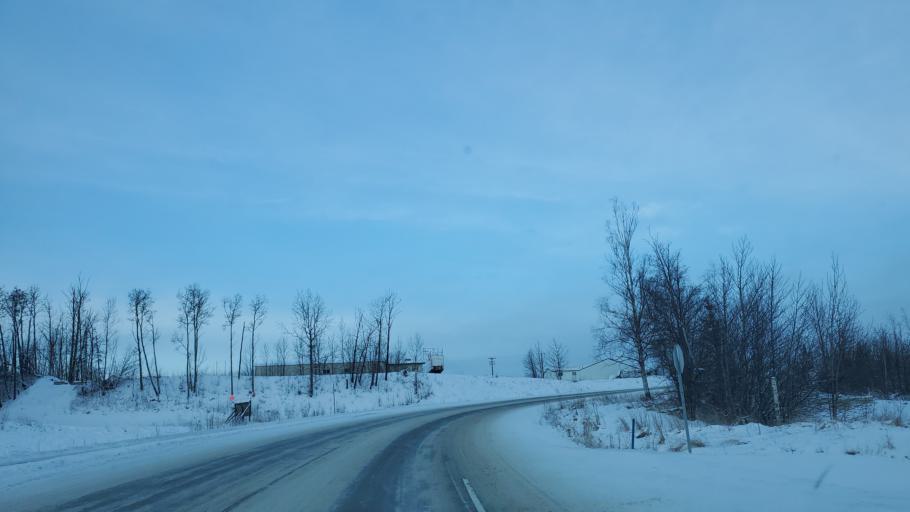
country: US
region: Alaska
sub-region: Matanuska-Susitna Borough
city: Gateway
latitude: 61.5598
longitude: -149.2723
